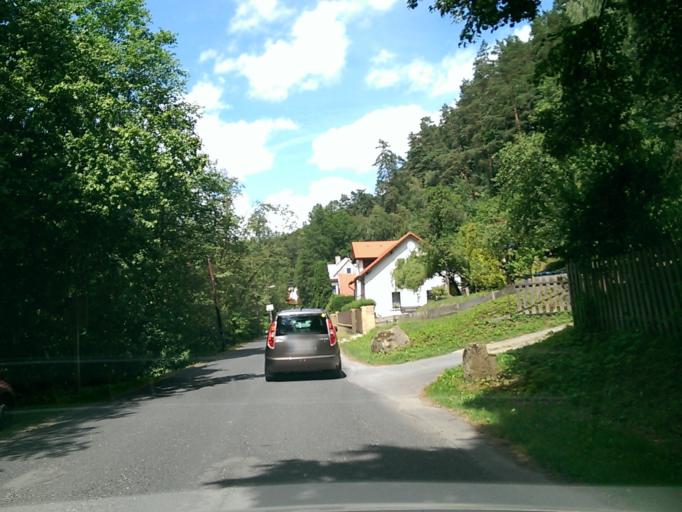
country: CZ
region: Central Bohemia
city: Mseno
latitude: 50.4372
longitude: 14.5806
